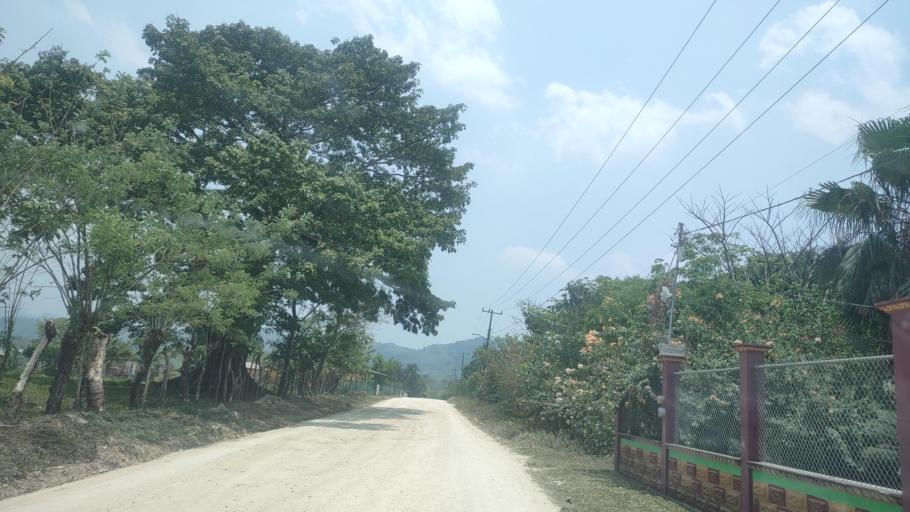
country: MX
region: Chiapas
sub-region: Tecpatan
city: Raudales Malpaso
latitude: 17.4592
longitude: -93.8034
